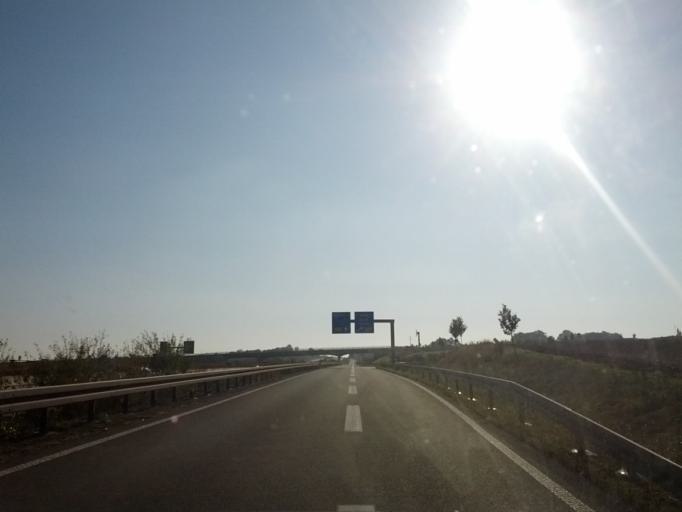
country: DE
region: Thuringia
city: Schwaara
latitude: 50.9048
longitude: 12.1222
